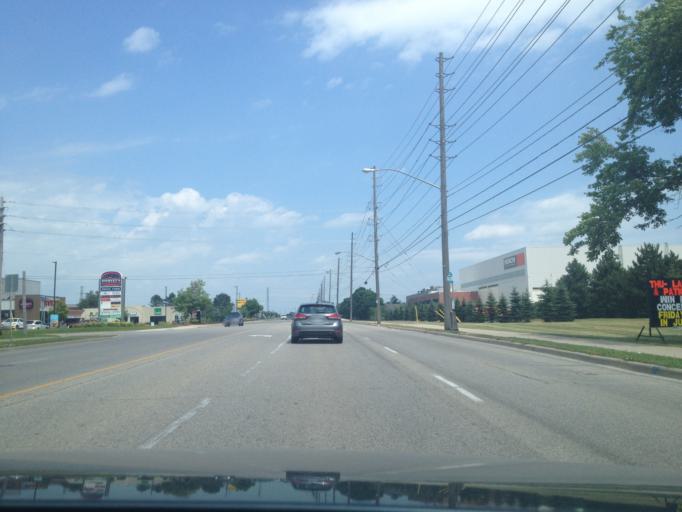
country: CA
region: Ontario
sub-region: Wellington County
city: Guelph
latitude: 43.5532
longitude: -80.2937
